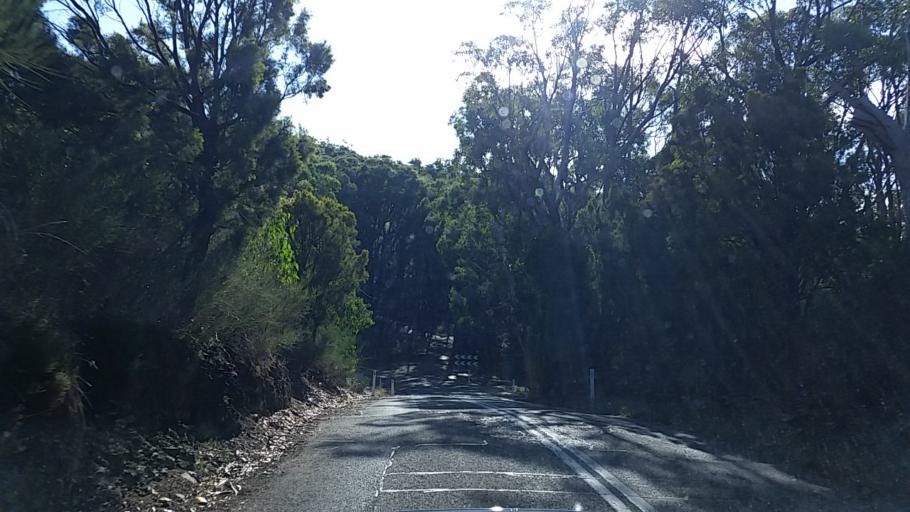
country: AU
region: South Australia
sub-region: Adelaide Hills
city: Crafers
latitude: -34.9697
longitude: 138.7134
